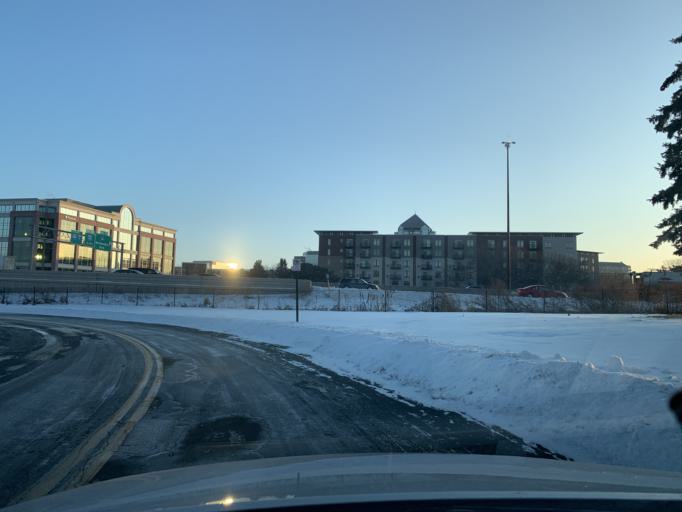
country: US
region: Minnesota
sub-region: Hennepin County
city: Edina
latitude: 44.8598
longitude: -93.3557
